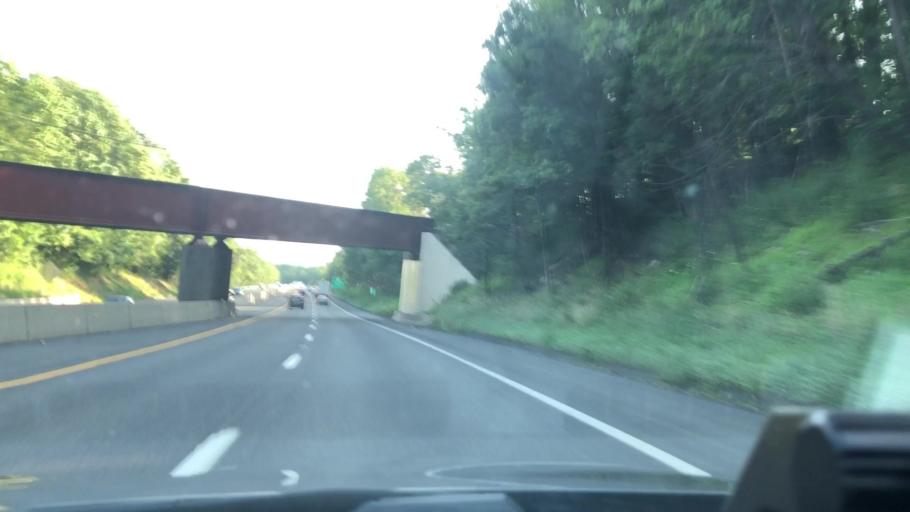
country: US
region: Pennsylvania
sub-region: Northampton County
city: Wind Gap
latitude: 40.8536
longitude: -75.3008
